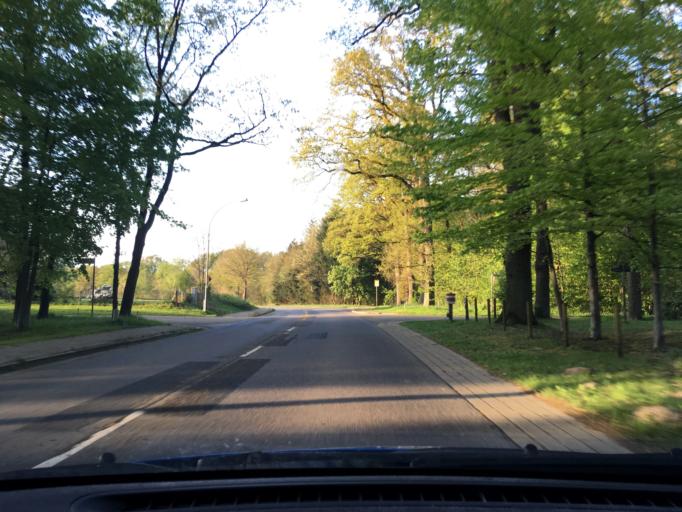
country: DE
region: Lower Saxony
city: Bispingen
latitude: 53.0288
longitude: 9.9991
